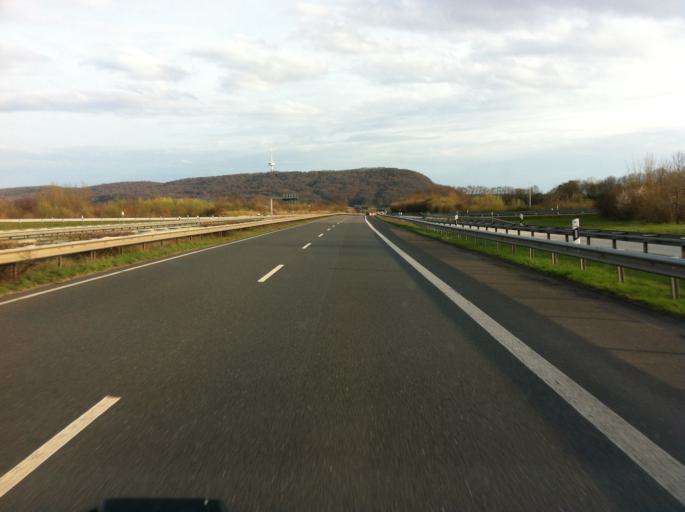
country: DE
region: North Rhine-Westphalia
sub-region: Regierungsbezirk Detmold
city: Minden
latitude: 52.2662
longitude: 8.9122
